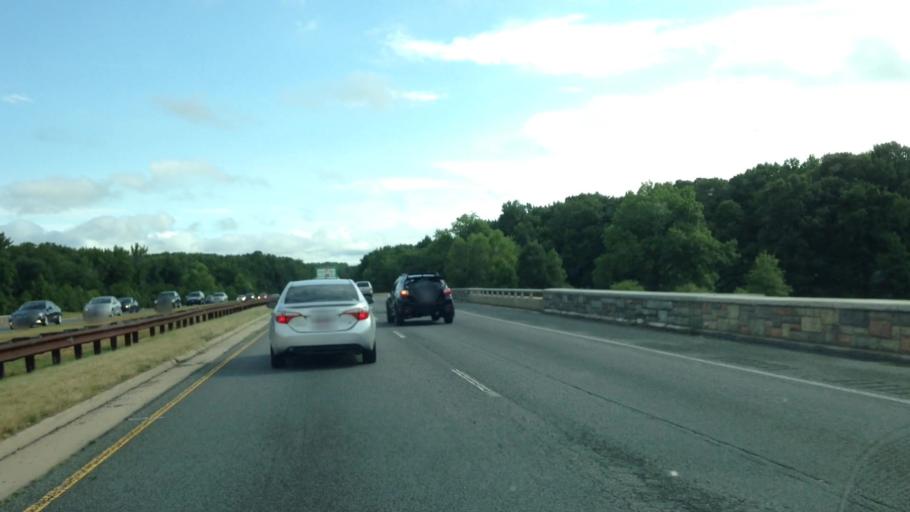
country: US
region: Maryland
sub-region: Prince George's County
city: Greenbelt
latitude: 39.0330
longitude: -76.8522
